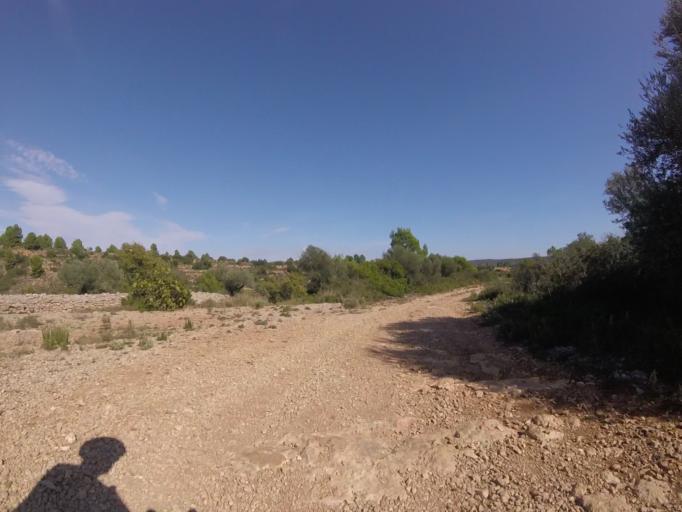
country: ES
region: Valencia
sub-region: Provincia de Castello
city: Cuevas de Vinroma
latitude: 40.2825
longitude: 0.0799
